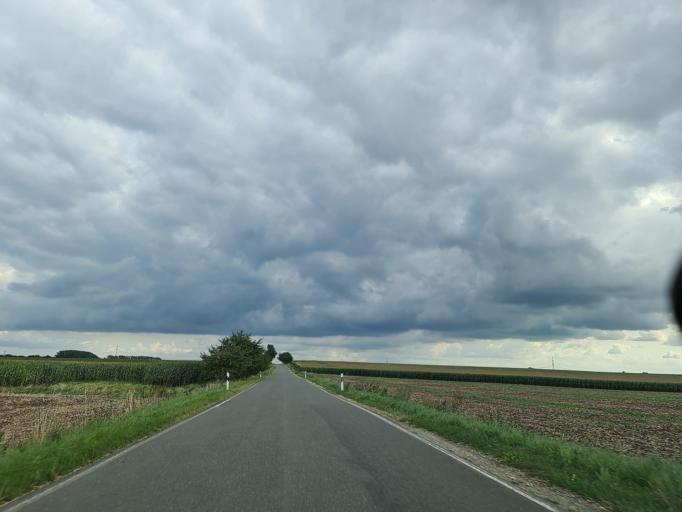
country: DE
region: Thuringia
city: Walpernhain
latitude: 51.0379
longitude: 11.9693
